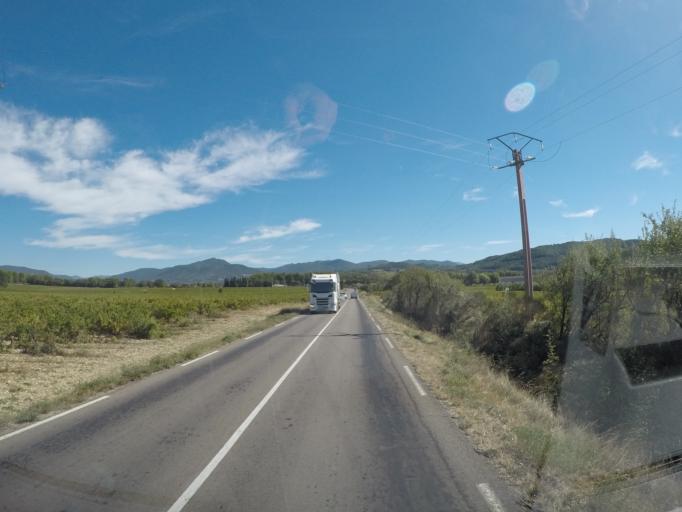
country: FR
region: Rhone-Alpes
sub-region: Departement de la Drome
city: Vinsobres
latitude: 44.3095
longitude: 5.0356
